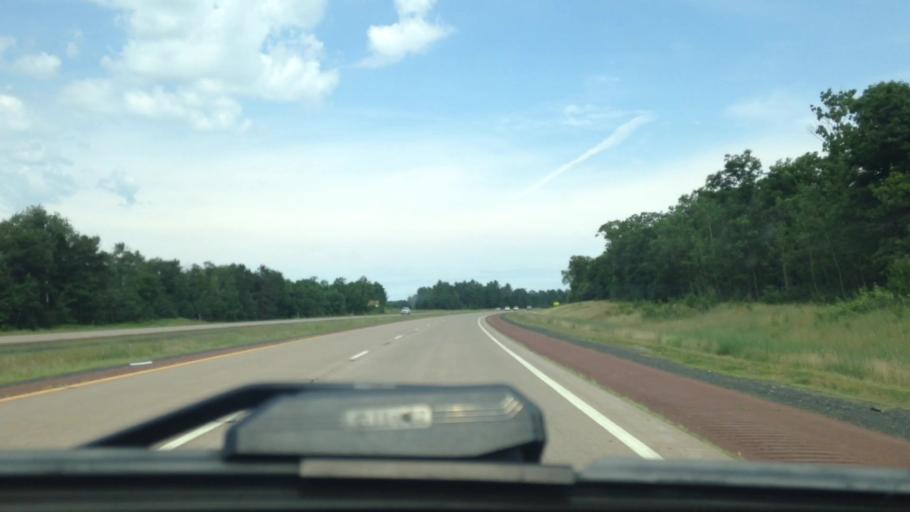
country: US
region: Wisconsin
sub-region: Douglas County
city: Lake Nebagamon
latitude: 46.3363
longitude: -91.8296
